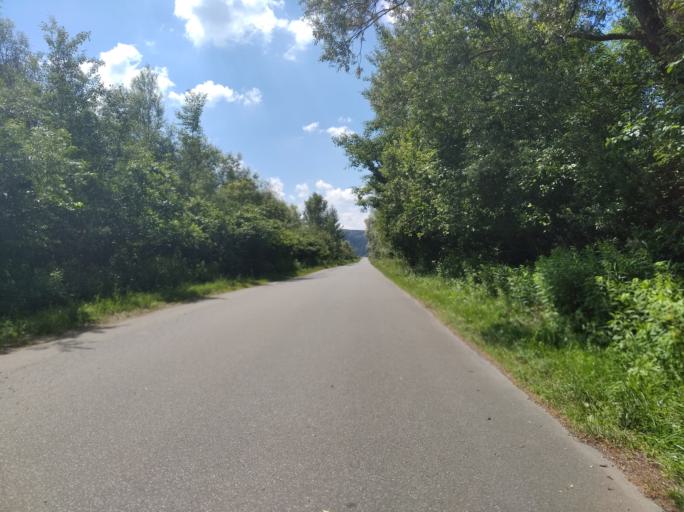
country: PL
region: Subcarpathian Voivodeship
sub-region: Powiat brzozowski
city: Dydnia
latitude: 49.7081
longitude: 22.2096
